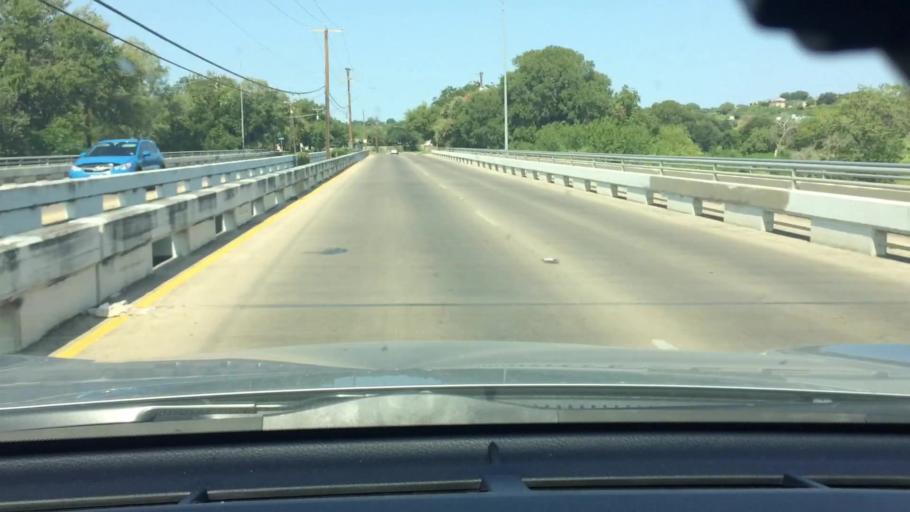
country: US
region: Texas
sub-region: Bexar County
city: China Grove
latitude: 29.3747
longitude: -98.4255
